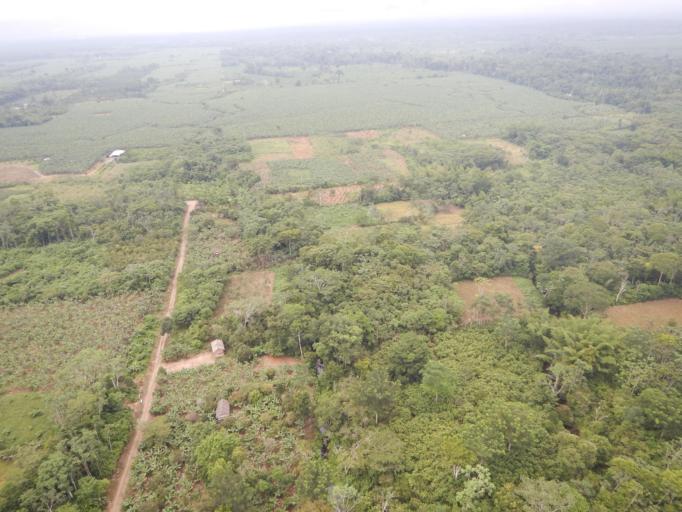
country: BO
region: Cochabamba
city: Chimore
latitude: -17.1141
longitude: -64.8410
